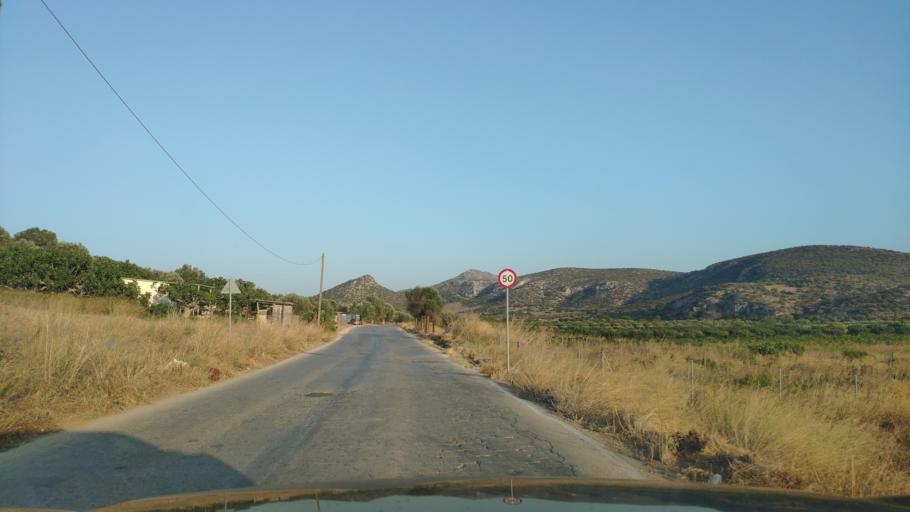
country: GR
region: Attica
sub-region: Nomarchia Anatolikis Attikis
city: Artemida
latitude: 37.9281
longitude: 23.9819
